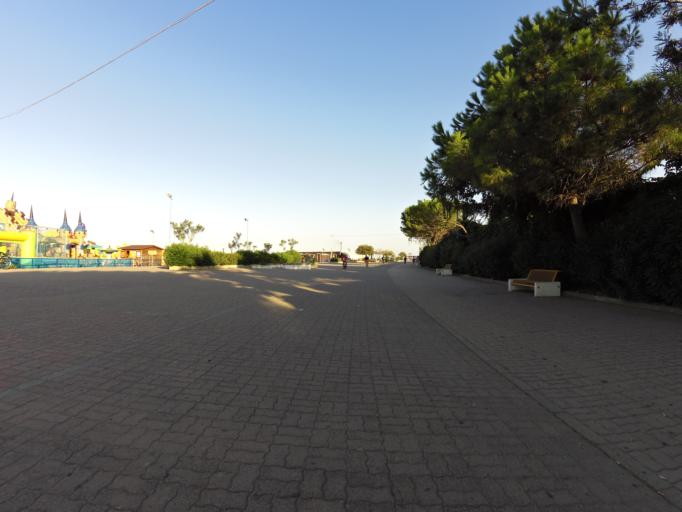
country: IT
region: Calabria
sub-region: Provincia di Catanzaro
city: Soverato Marina
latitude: 38.6895
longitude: 16.5541
